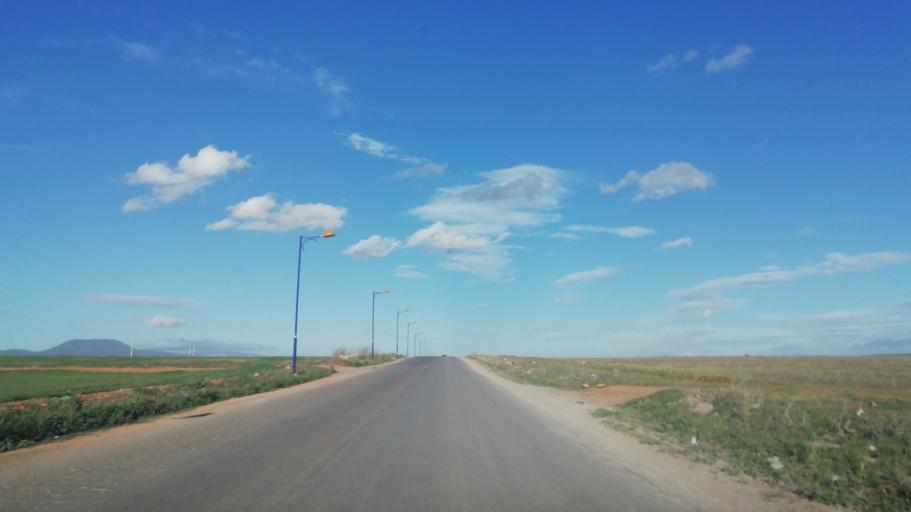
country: DZ
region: Oran
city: Sidi ech Chahmi
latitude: 35.6439
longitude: -0.5361
